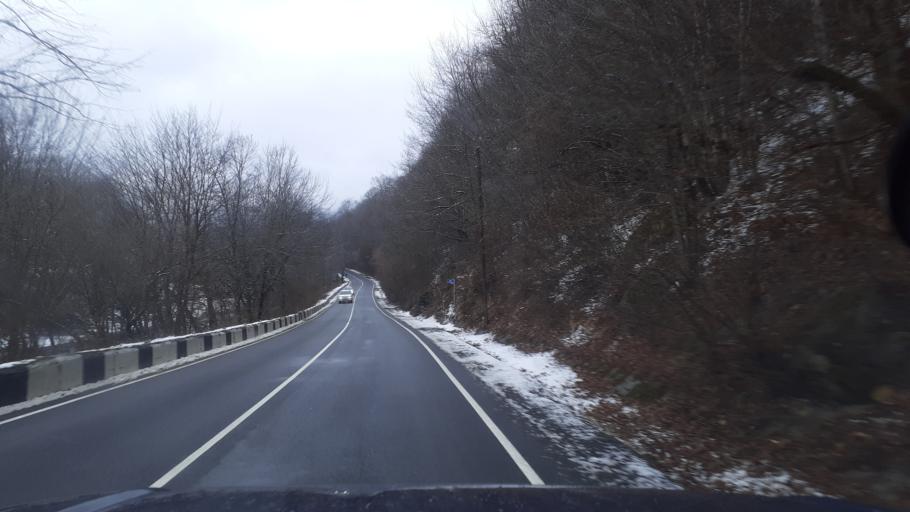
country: RU
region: Adygeya
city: Kamennomostskiy
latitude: 44.1199
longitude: 40.1225
